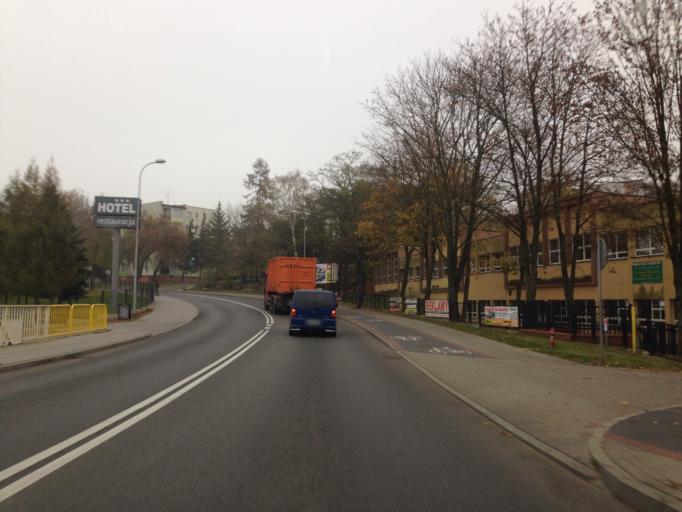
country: PL
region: Warmian-Masurian Voivodeship
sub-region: Powiat ilawski
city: Ilawa
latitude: 53.5976
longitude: 19.5561
